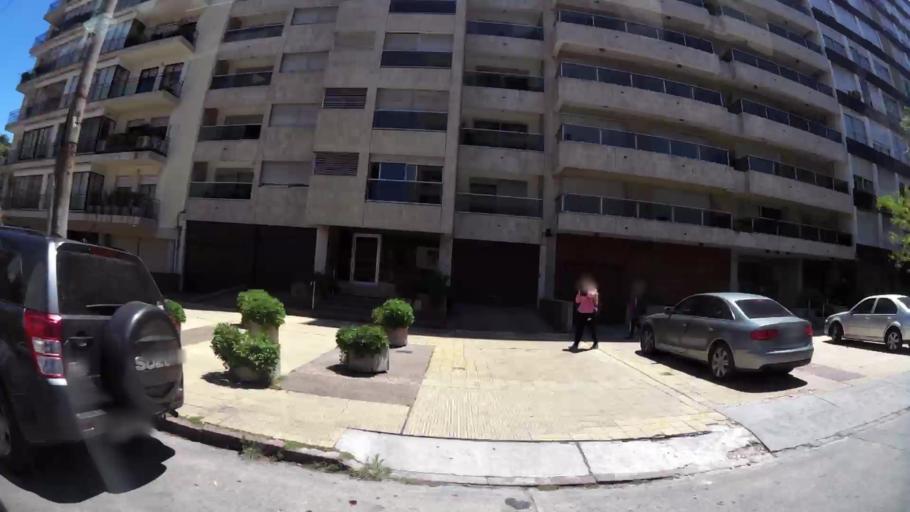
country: UY
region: Montevideo
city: Montevideo
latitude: -34.9034
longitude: -56.1619
